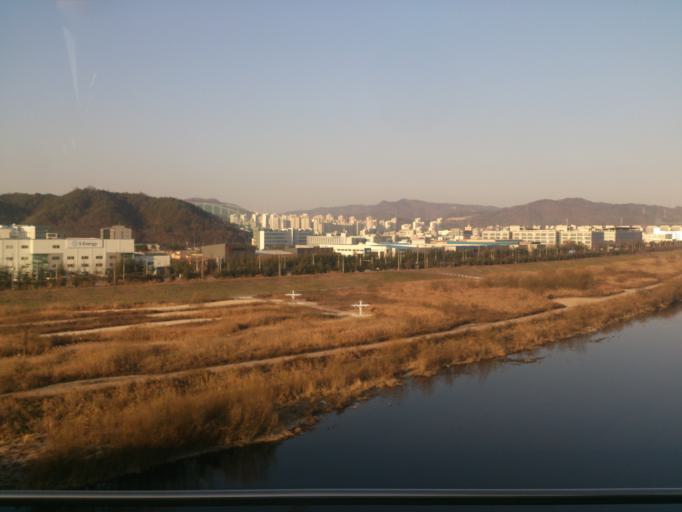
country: KR
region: Daejeon
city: Songgang-dong
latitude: 36.4206
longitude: 127.4159
